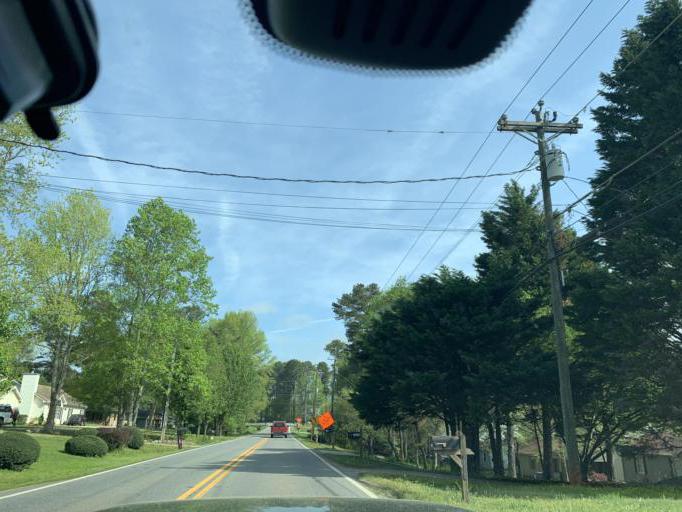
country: US
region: Georgia
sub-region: Forsyth County
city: Cumming
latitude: 34.2296
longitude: -84.0834
